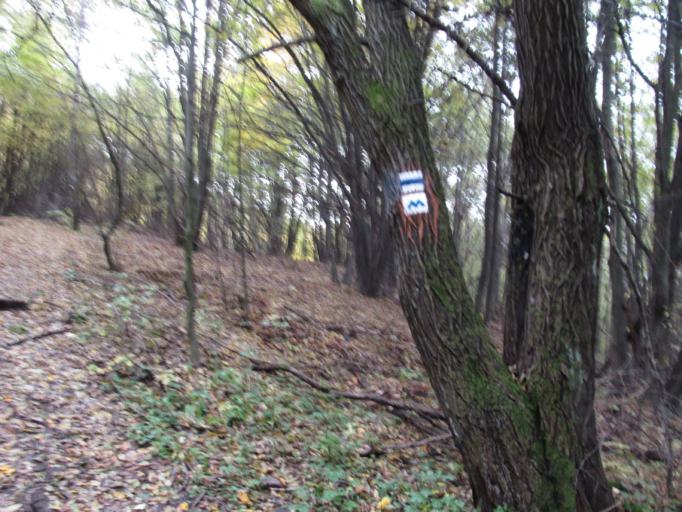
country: HU
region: Nograd
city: Batonyterenye
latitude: 47.9274
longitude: 19.8551
